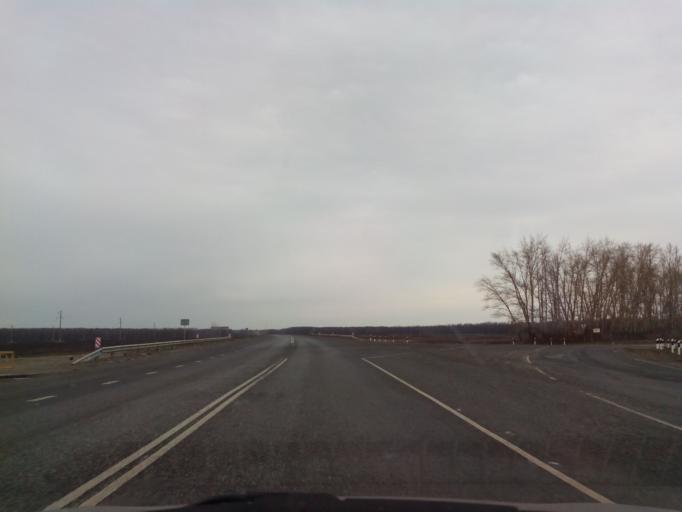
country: RU
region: Tambov
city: Zavoronezhskoye
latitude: 52.9883
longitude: 40.5580
